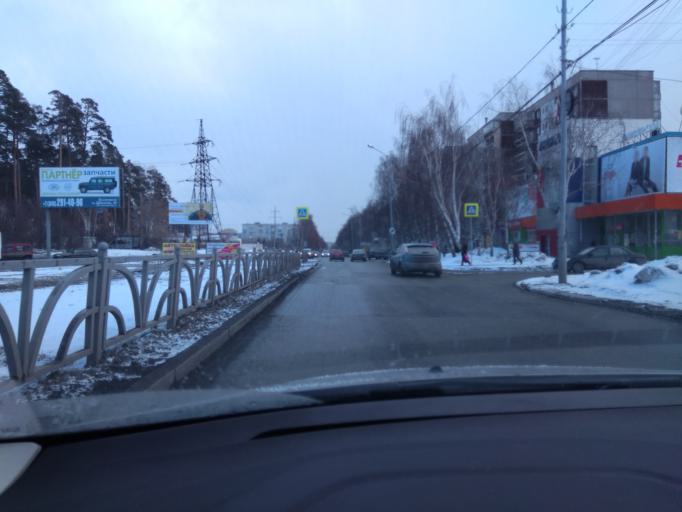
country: RU
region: Sverdlovsk
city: Sovkhoznyy
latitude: 56.8054
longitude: 60.5590
